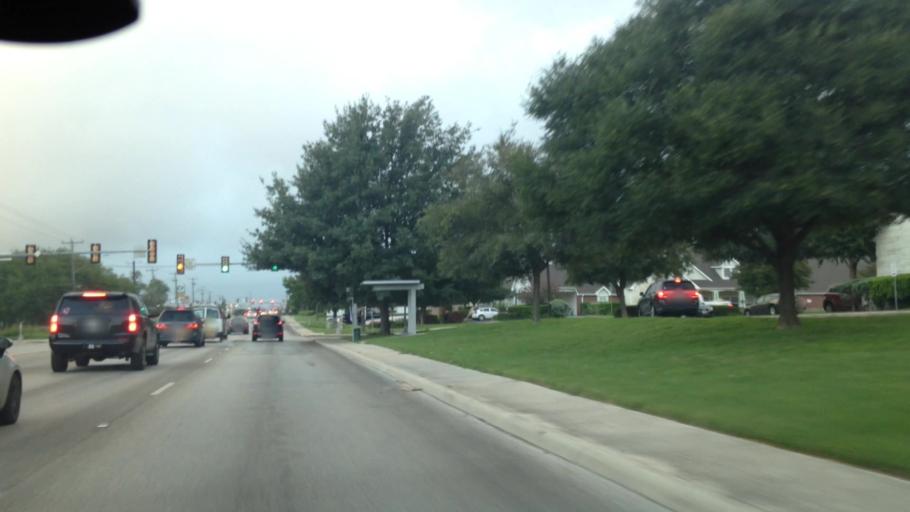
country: US
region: Texas
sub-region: Bexar County
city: Live Oak
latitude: 29.5741
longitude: -98.3779
